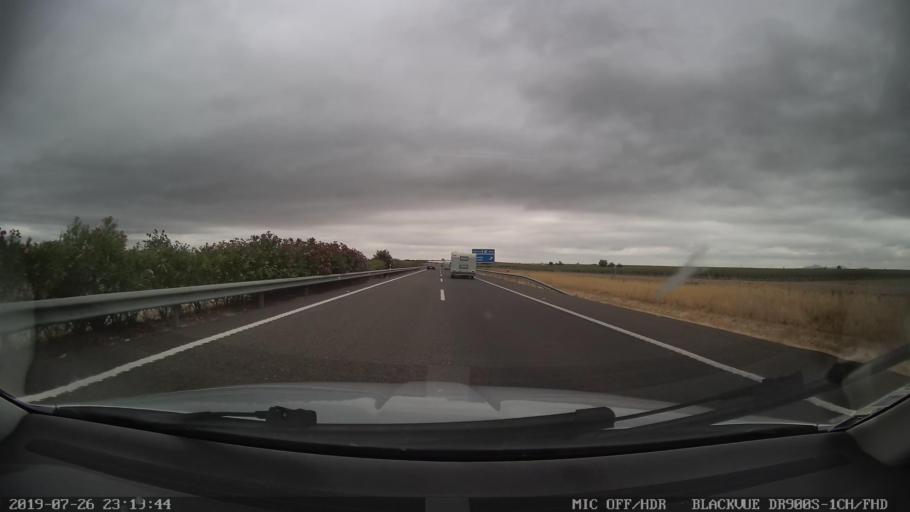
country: ES
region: Extremadura
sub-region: Provincia de Caceres
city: Miajadas
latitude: 39.1107
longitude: -5.9857
